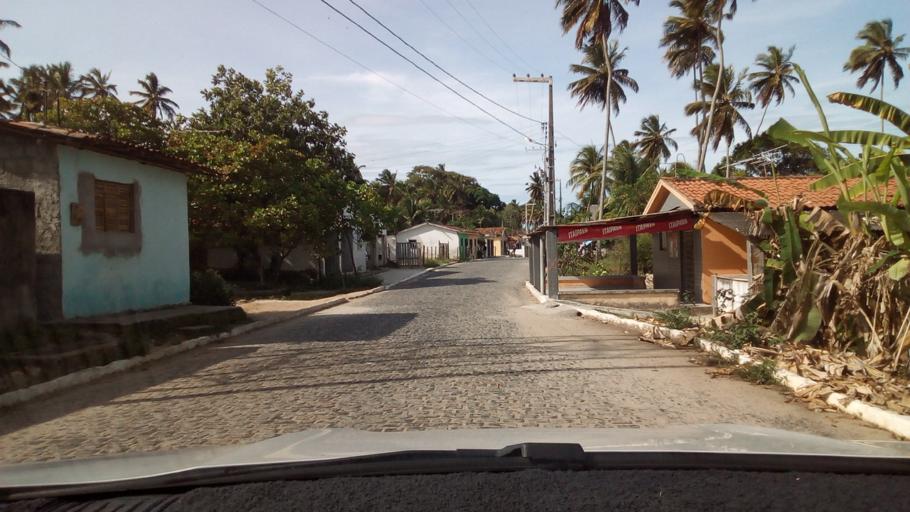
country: BR
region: Paraiba
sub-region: Cabedelo
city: Cabedelo
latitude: -7.0304
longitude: -34.8719
